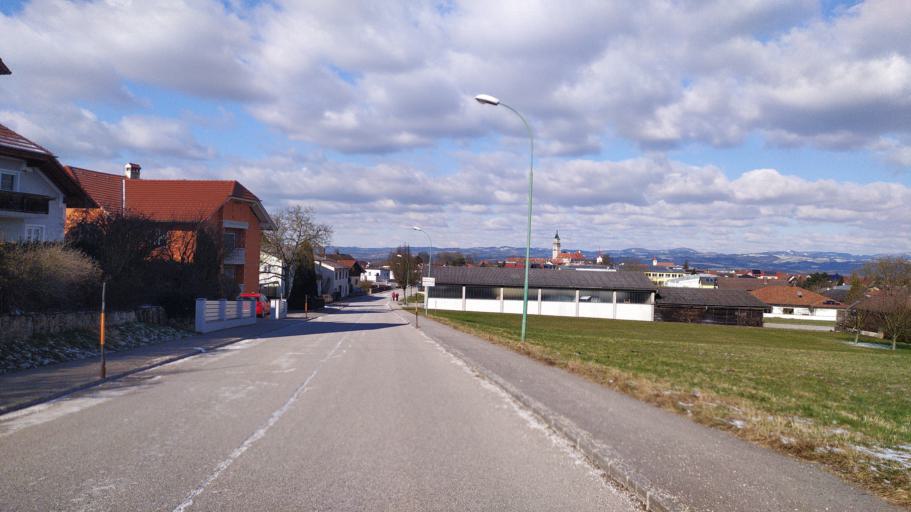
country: AT
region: Lower Austria
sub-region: Politischer Bezirk Amstetten
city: Strengberg
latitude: 48.1600
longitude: 14.7163
